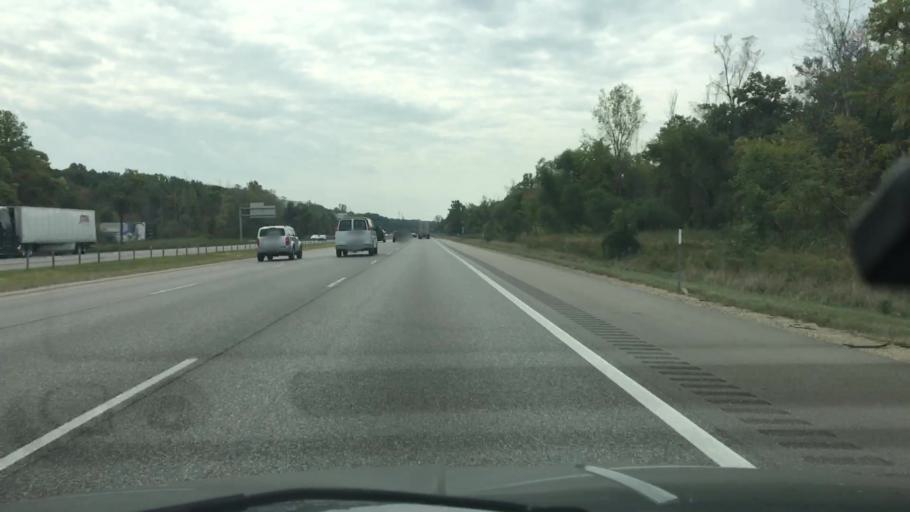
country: US
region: Michigan
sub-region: Berrien County
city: Stevensville
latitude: 41.9940
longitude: -86.5386
